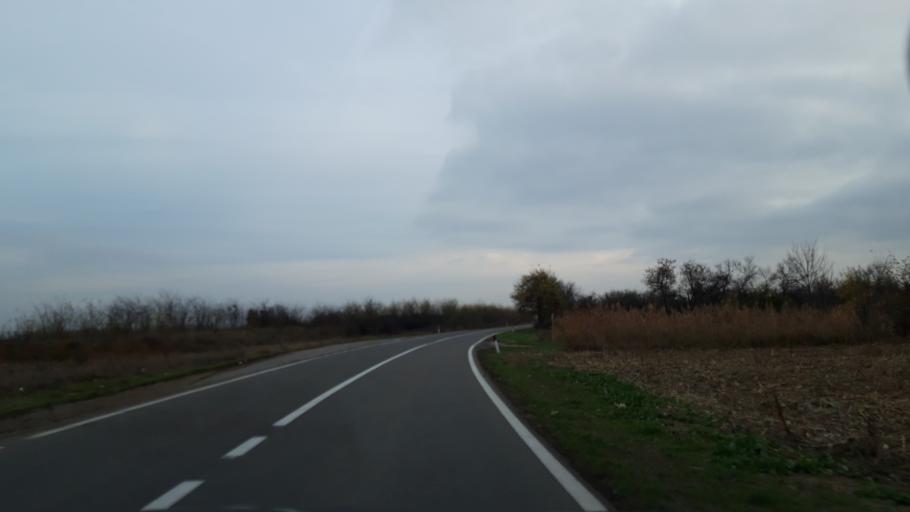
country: RS
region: Autonomna Pokrajina Vojvodina
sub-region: Severnobanatski Okrug
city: Coka
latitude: 45.9620
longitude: 20.1324
